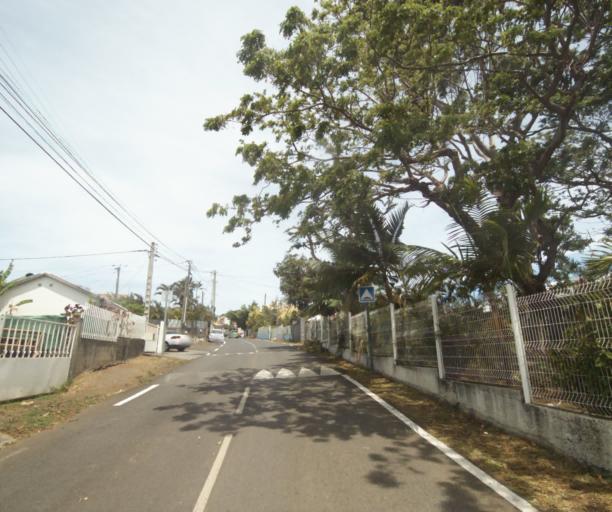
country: RE
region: Reunion
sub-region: Reunion
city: Saint-Paul
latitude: -21.0473
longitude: 55.2652
